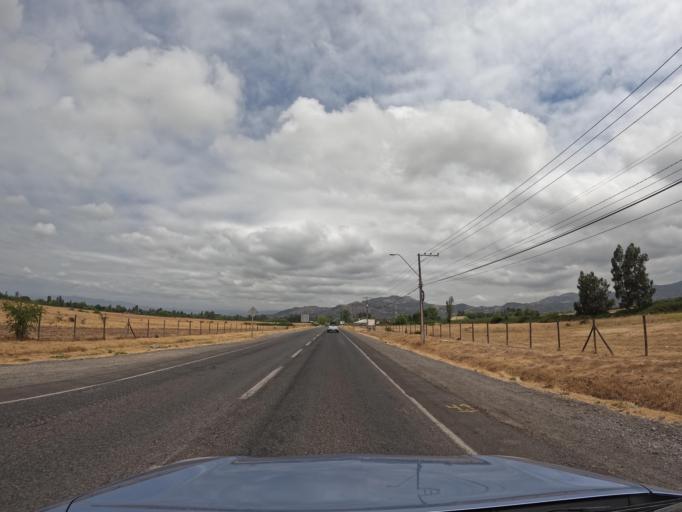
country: CL
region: Maule
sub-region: Provincia de Curico
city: Teno
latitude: -34.8640
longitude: -71.1759
